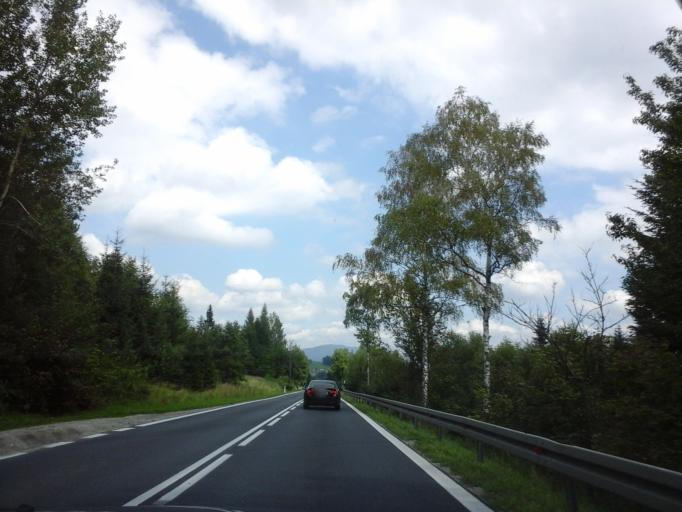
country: PL
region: Lesser Poland Voivodeship
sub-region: Powiat nowotarski
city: Sieniawa
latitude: 49.5579
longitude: 19.9400
